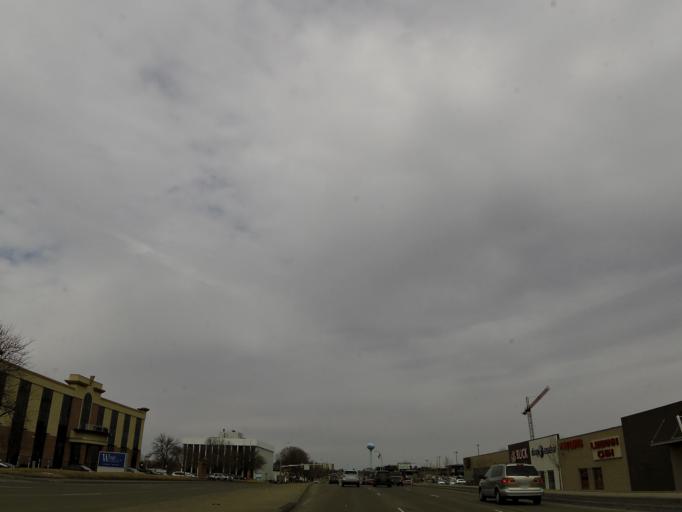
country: US
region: Minnesota
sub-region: Hennepin County
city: Edina
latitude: 44.8697
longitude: -93.3290
